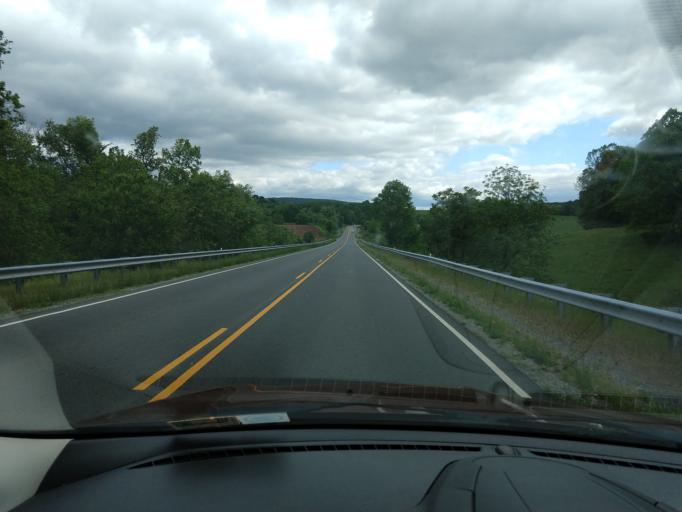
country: US
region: Virginia
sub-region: Wythe County
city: Wytheville
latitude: 36.8861
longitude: -80.9778
